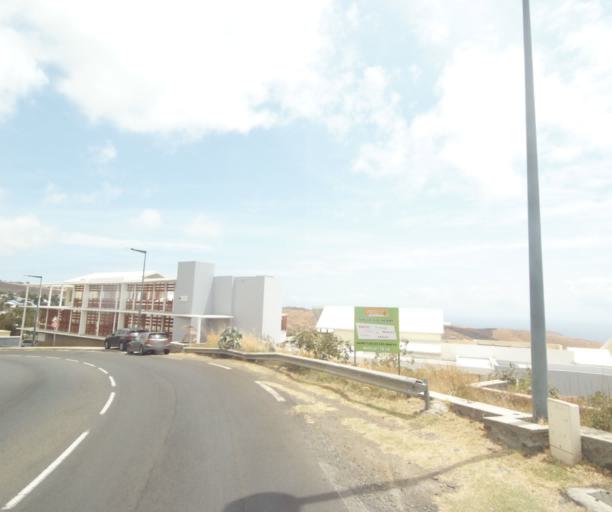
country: RE
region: Reunion
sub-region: Reunion
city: Saint-Paul
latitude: -21.0276
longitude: 55.2679
